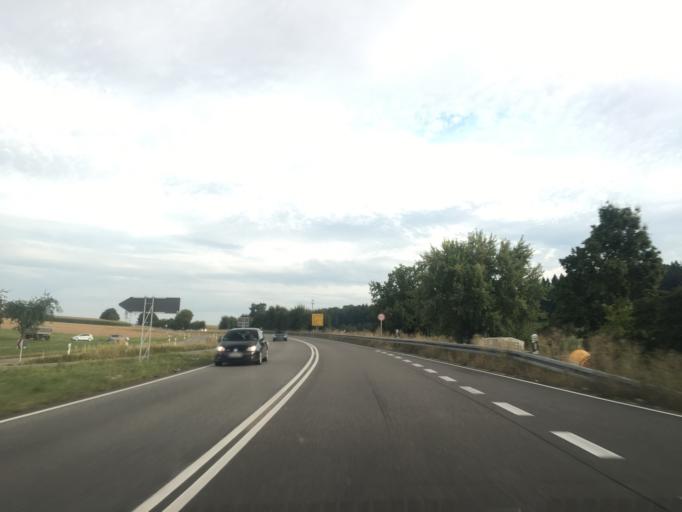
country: DE
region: Baden-Wuerttemberg
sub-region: Regierungsbezirk Stuttgart
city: Neckartailfingen
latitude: 48.6186
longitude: 9.2483
